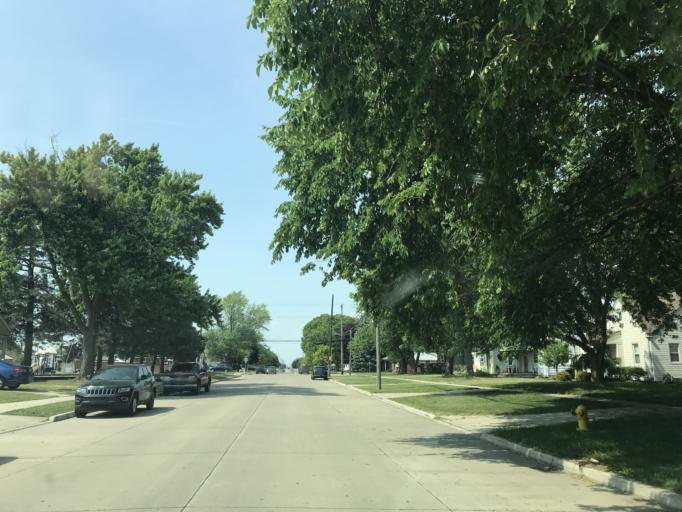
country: US
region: Michigan
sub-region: Wayne County
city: Riverview
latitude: 42.1788
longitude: -83.1793
